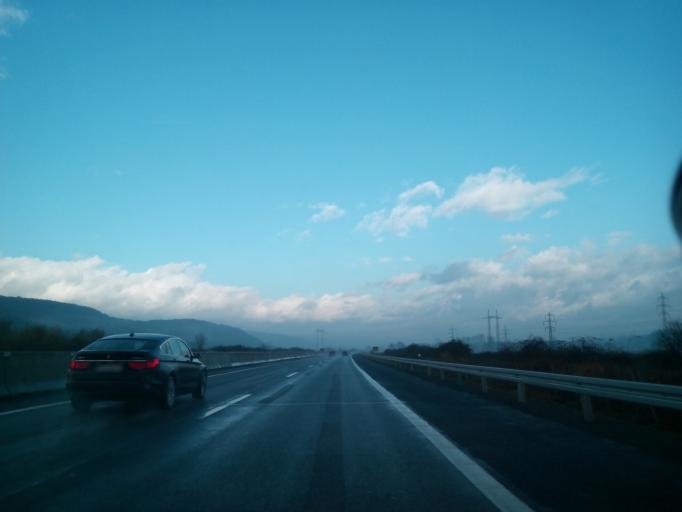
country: SK
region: Presovsky
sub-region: Okres Presov
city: Presov
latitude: 48.8805
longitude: 21.2512
